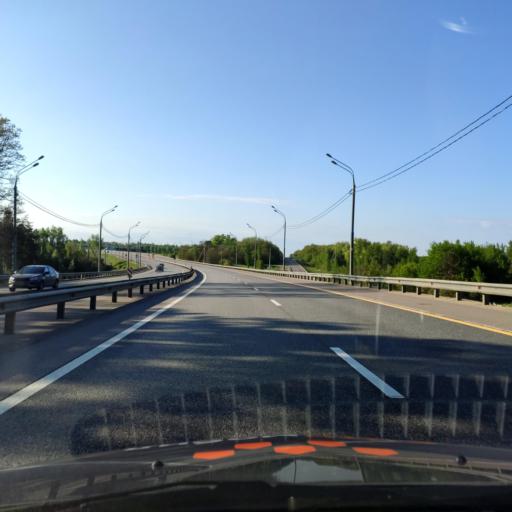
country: RU
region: Lipetsk
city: Khlevnoye
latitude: 52.2440
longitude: 39.0670
